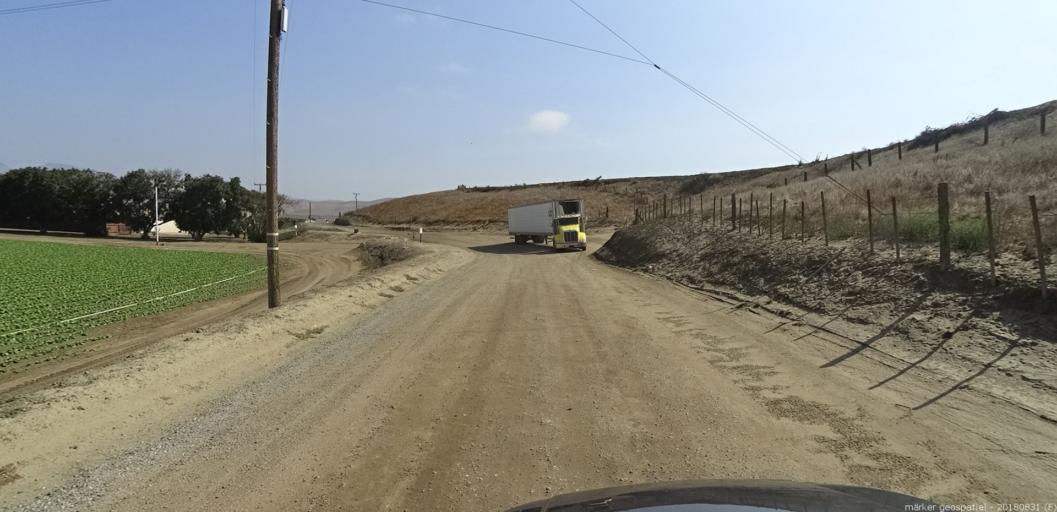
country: US
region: California
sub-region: Monterey County
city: Greenfield
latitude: 36.3077
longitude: -121.2020
